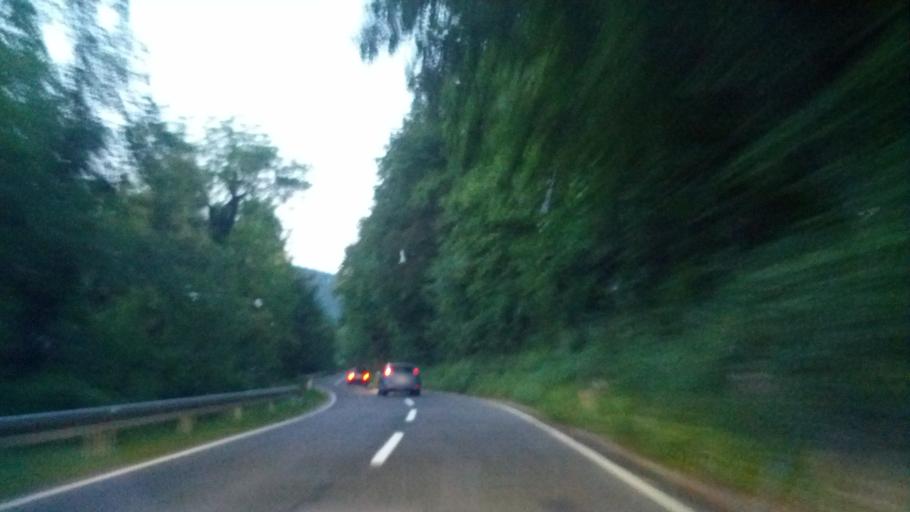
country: BA
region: Federation of Bosnia and Herzegovina
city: Bosanska Krupa
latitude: 44.8716
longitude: 16.1108
